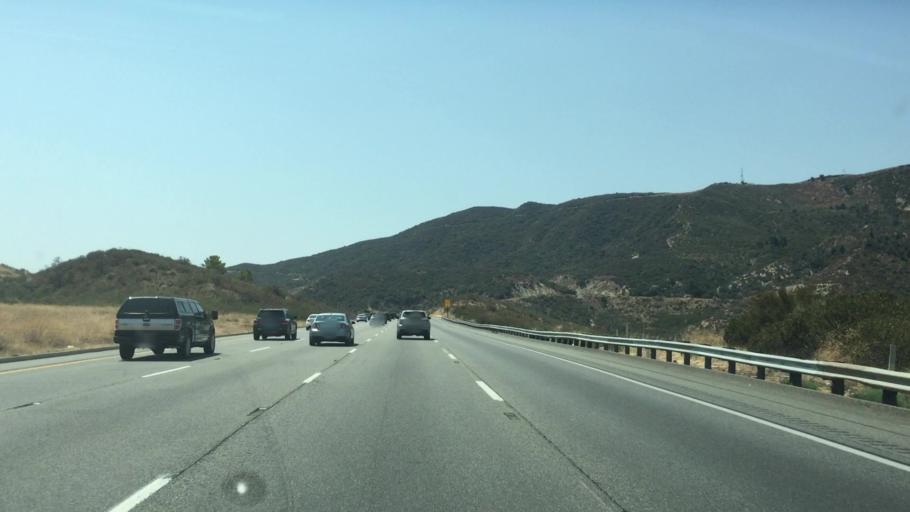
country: US
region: California
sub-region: Los Angeles County
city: Castaic
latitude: 34.5986
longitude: -118.7117
